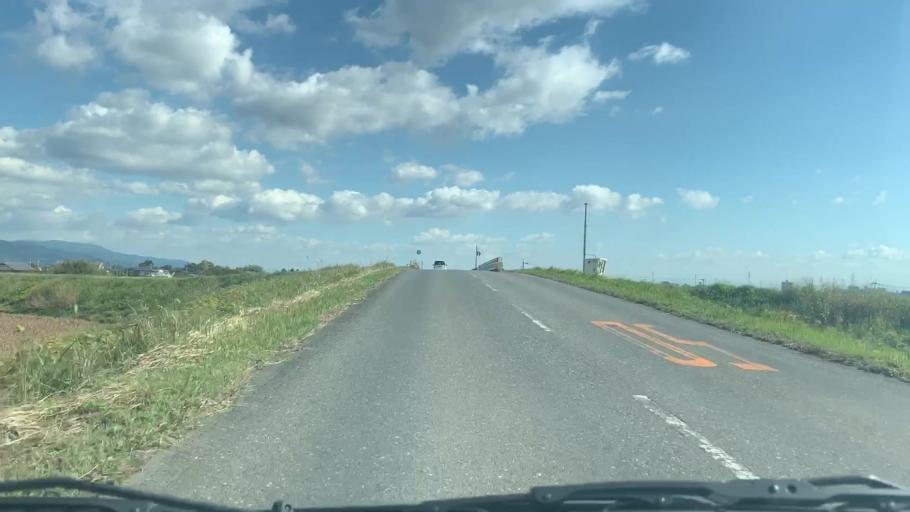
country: JP
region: Saga Prefecture
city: Saga-shi
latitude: 33.2833
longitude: 130.2427
